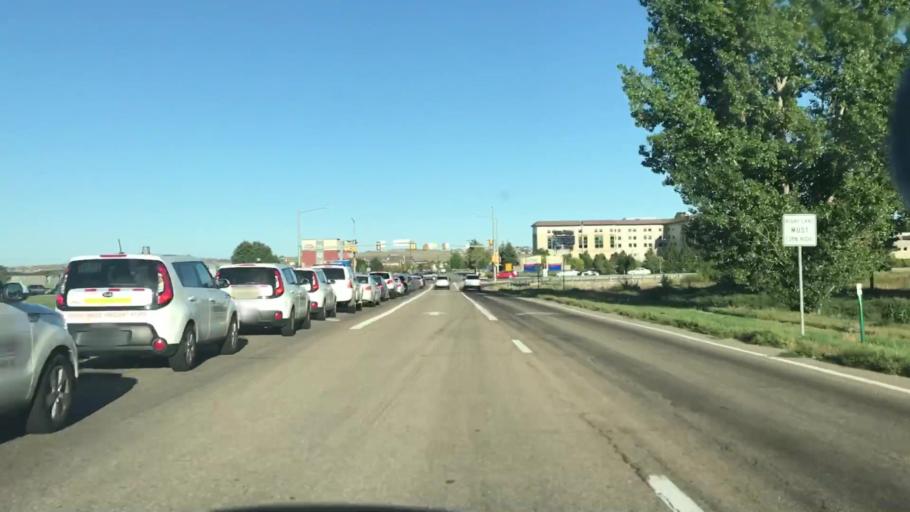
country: US
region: Colorado
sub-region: Boulder County
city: Lafayette
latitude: 39.9724
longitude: -105.0920
